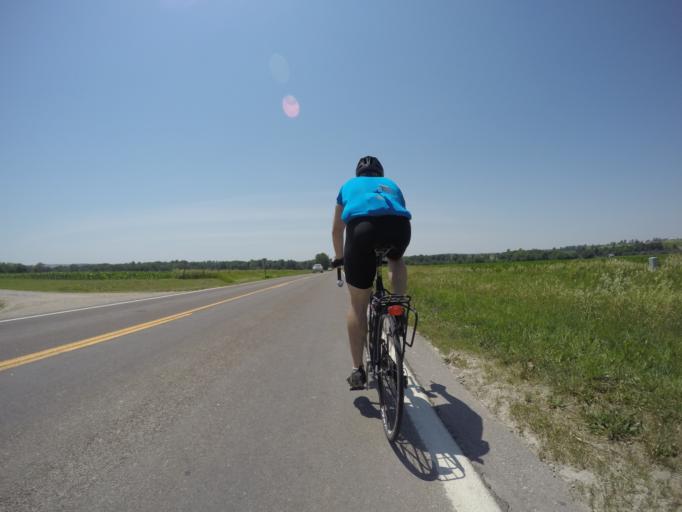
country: US
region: Nebraska
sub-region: Pawnee County
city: Pawnee City
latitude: 40.0317
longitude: -96.0481
